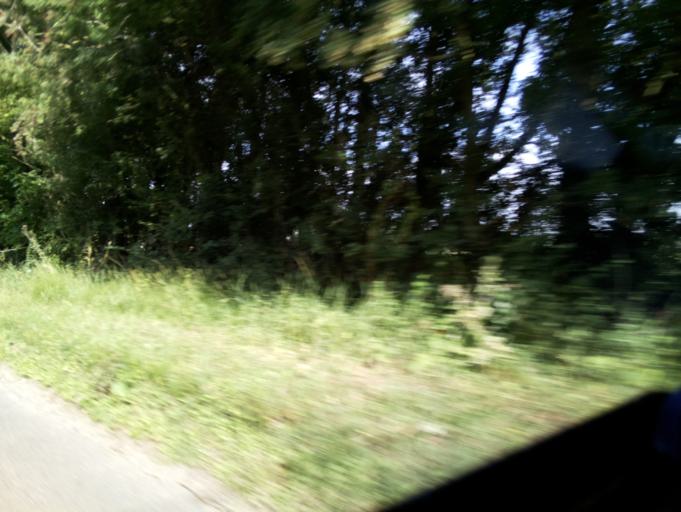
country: GB
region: England
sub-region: Oxfordshire
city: Shrivenham
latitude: 51.6438
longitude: -1.6398
